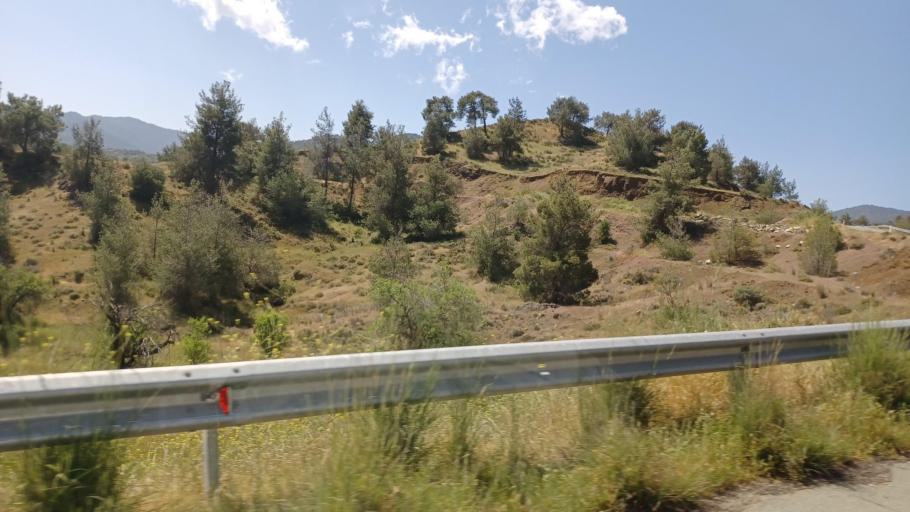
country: CY
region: Lefkosia
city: Astromeritis
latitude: 35.0536
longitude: 33.0240
